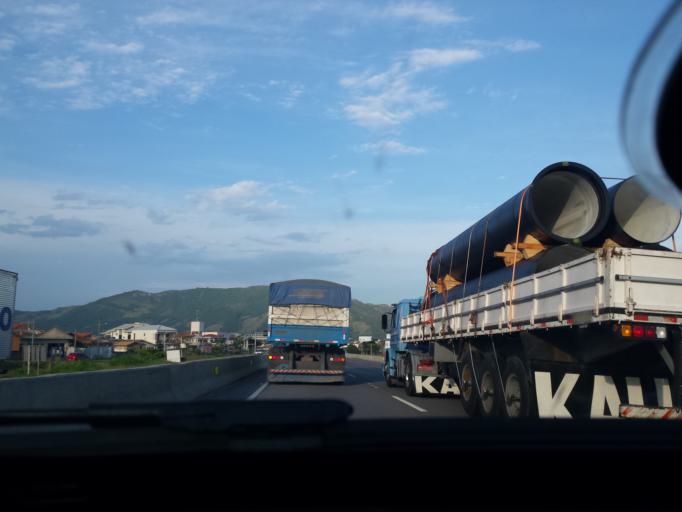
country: BR
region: Santa Catarina
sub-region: Laguna
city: Laguna
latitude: -28.4408
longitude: -48.8180
